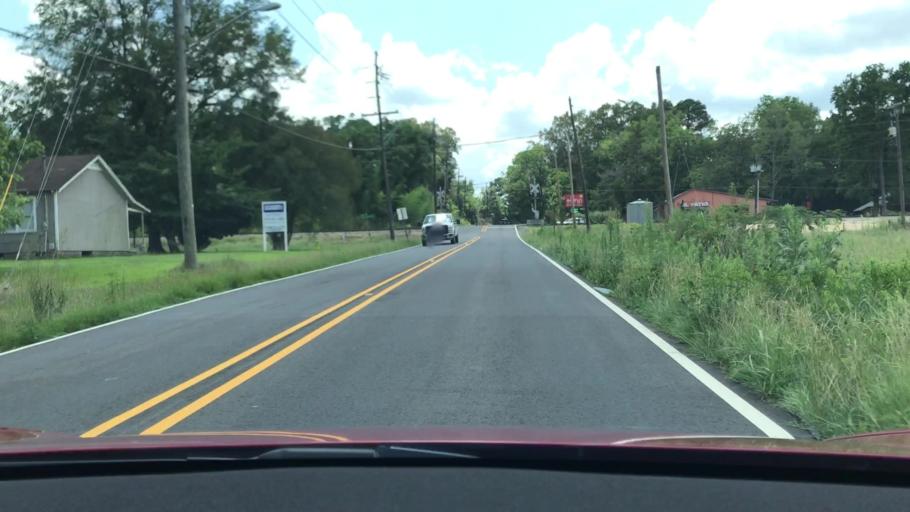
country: US
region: Louisiana
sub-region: Bossier Parish
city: Bossier City
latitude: 32.3921
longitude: -93.7296
